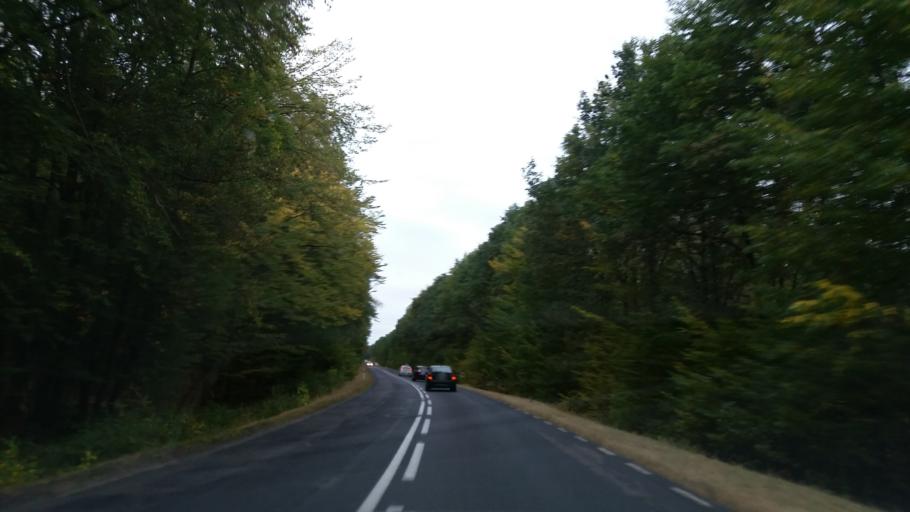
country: PL
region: Lubusz
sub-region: Powiat gorzowski
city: Klodawa
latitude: 52.8555
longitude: 15.1996
